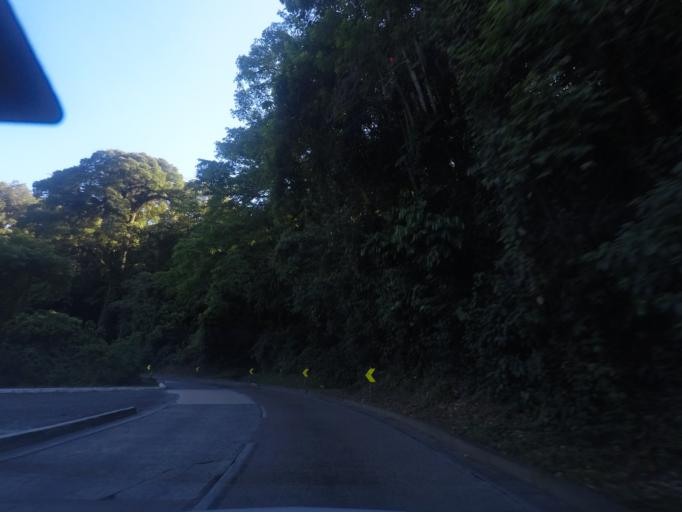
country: BR
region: Rio de Janeiro
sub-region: Petropolis
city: Petropolis
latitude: -22.5639
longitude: -43.2360
